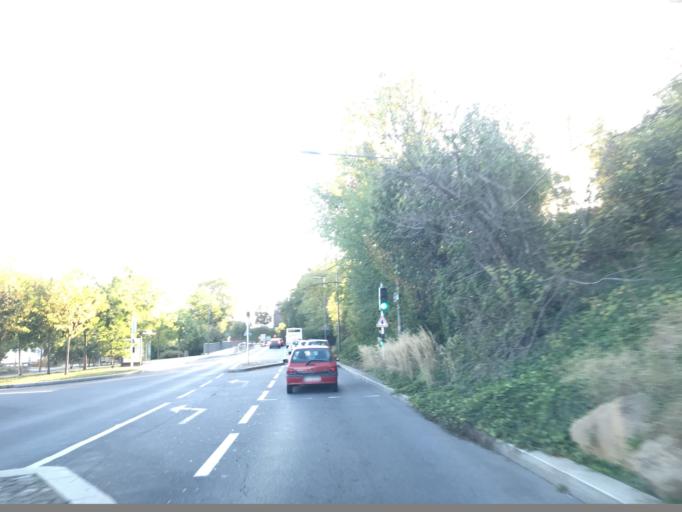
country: FR
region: Lorraine
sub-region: Departement de la Moselle
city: Metz
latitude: 49.1139
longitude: 6.1864
